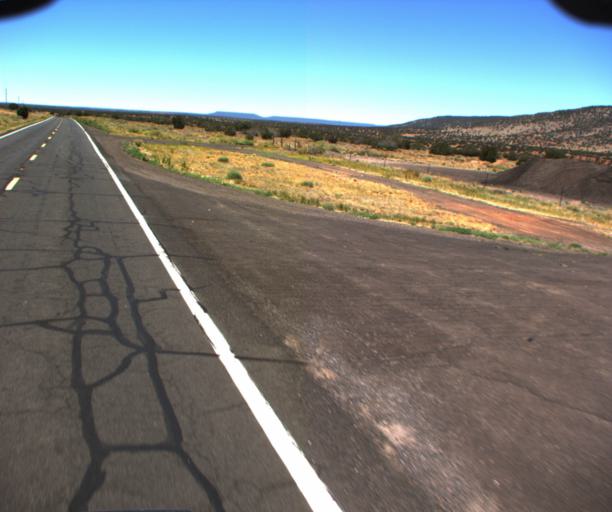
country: US
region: Arizona
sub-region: Coconino County
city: LeChee
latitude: 34.8661
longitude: -110.9082
